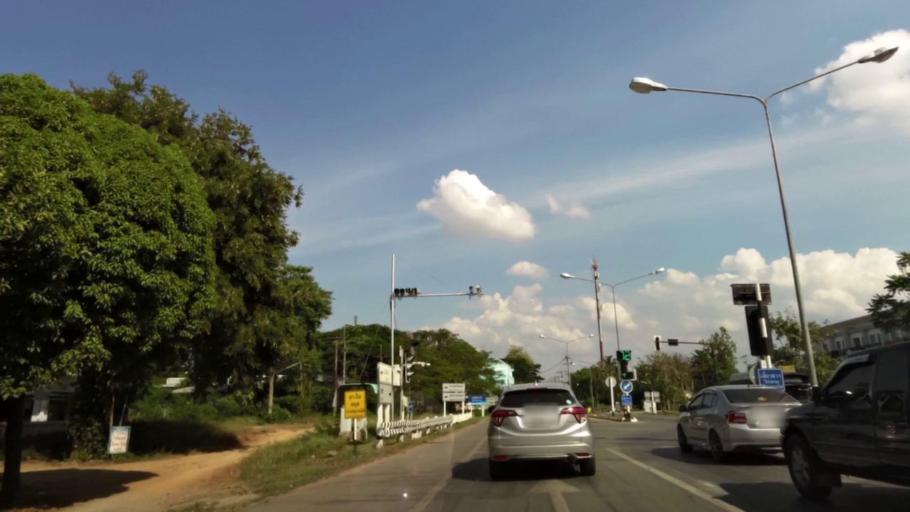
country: TH
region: Phrae
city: Phrae
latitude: 18.1352
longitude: 100.1313
